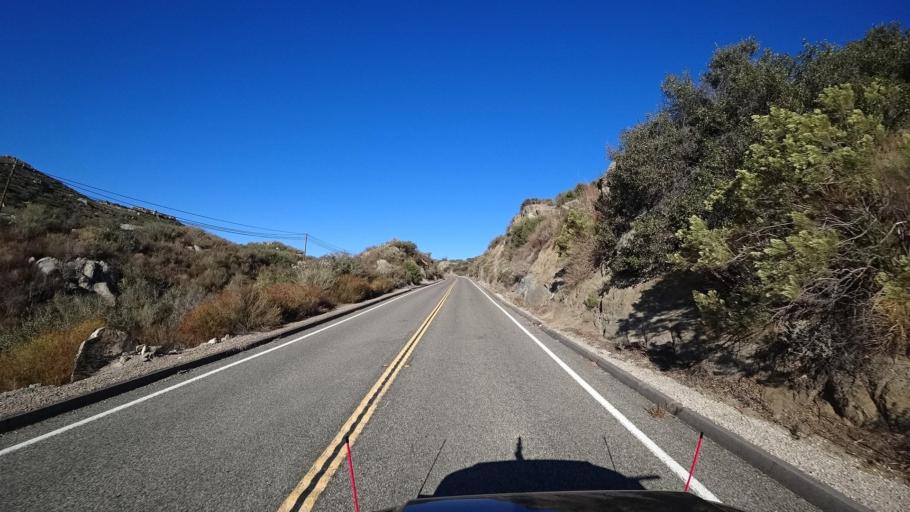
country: MX
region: Baja California
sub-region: Tecate
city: Hacienda Tecate
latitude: 32.5991
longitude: -116.5717
